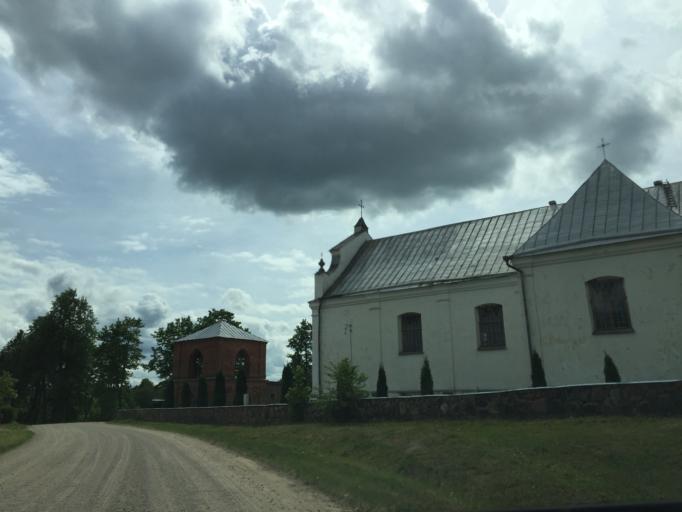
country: LV
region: Dagda
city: Dagda
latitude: 56.0280
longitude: 27.6213
